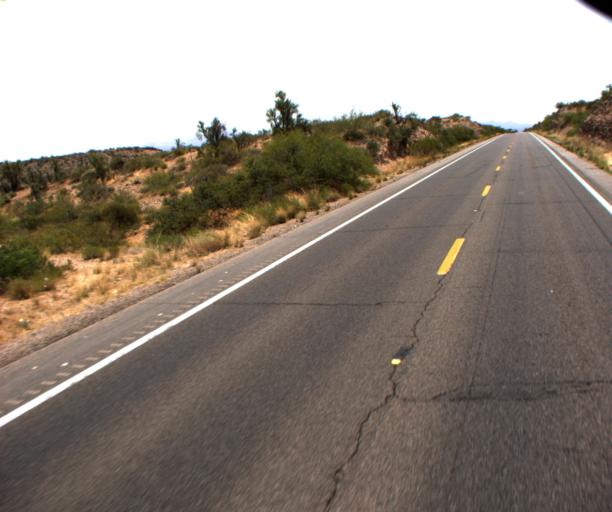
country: US
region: Arizona
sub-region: Gila County
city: Peridot
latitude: 33.3251
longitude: -110.5516
